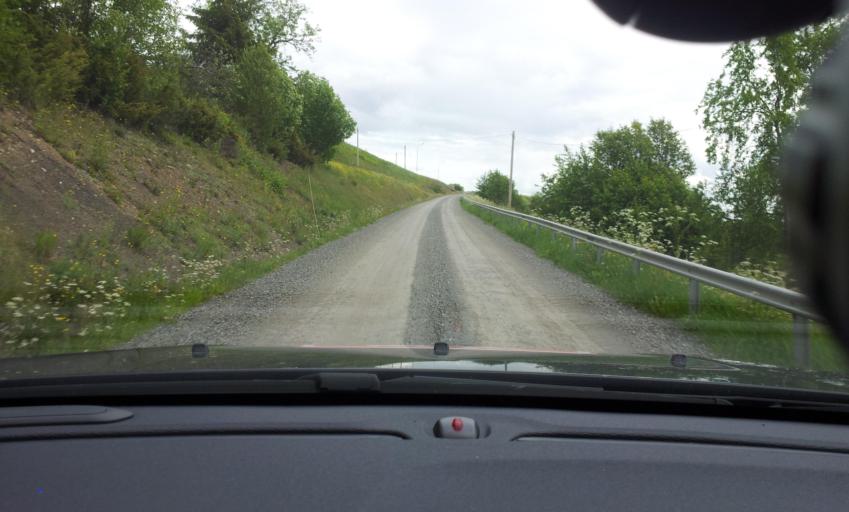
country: SE
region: Jaemtland
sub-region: OEstersunds Kommun
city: Brunflo
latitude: 62.9657
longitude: 14.7037
